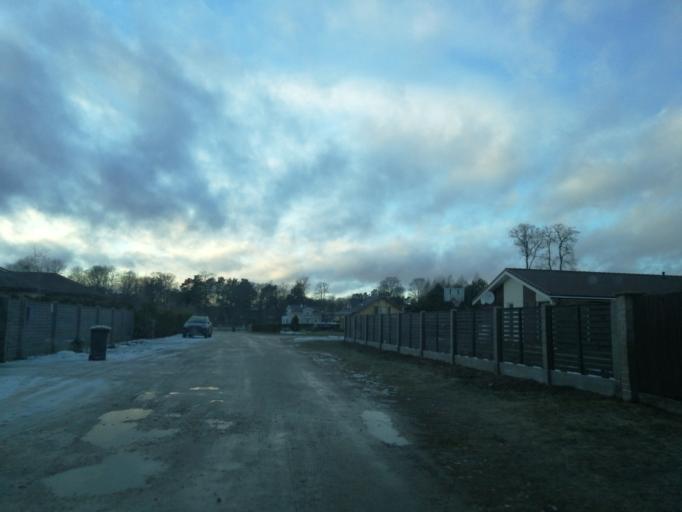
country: LV
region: Adazi
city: Adazi
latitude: 57.0745
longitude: 24.3473
